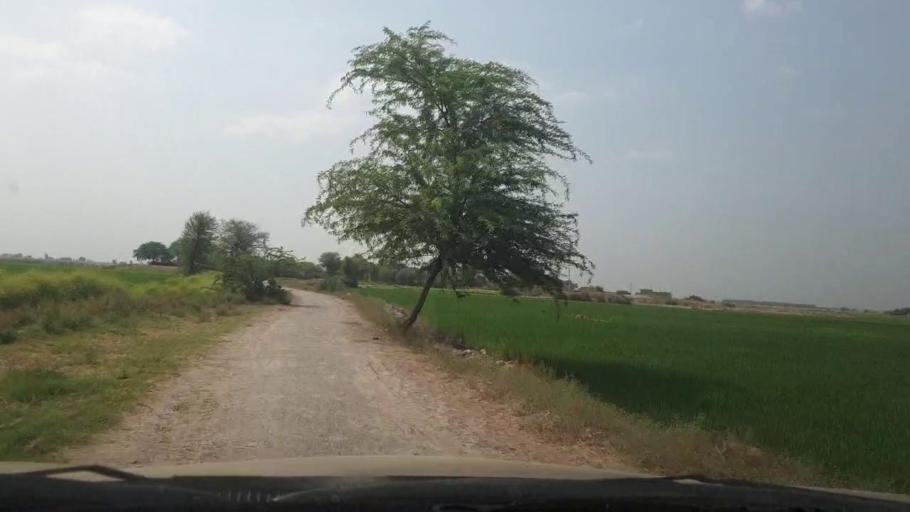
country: PK
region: Sindh
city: Larkana
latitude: 27.6826
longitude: 68.2023
